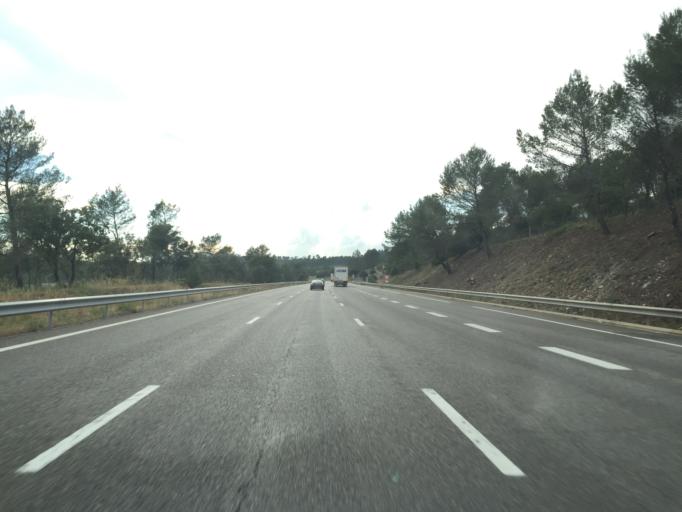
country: FR
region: Provence-Alpes-Cote d'Azur
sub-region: Departement du Var
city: La Celle
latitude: 43.4237
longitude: 5.9867
